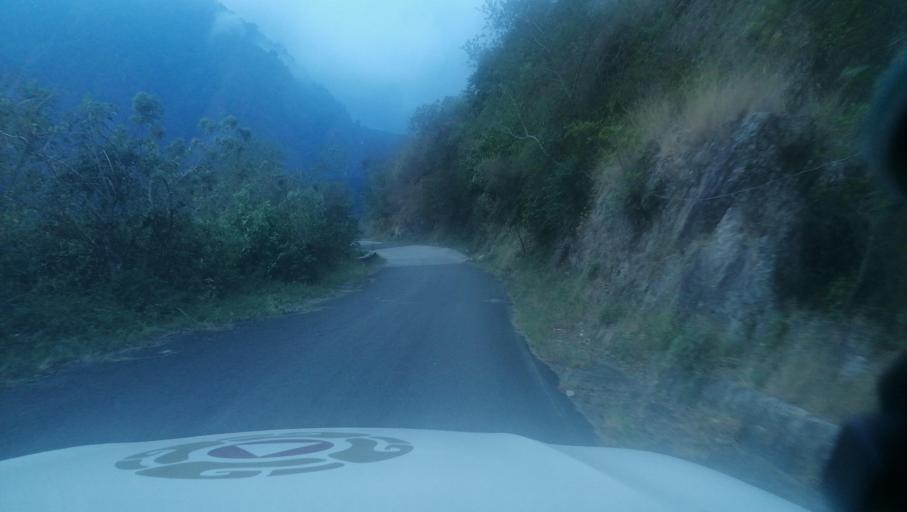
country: MX
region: Chiapas
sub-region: Cacahoatan
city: Benito Juarez
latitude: 15.1415
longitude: -92.1944
